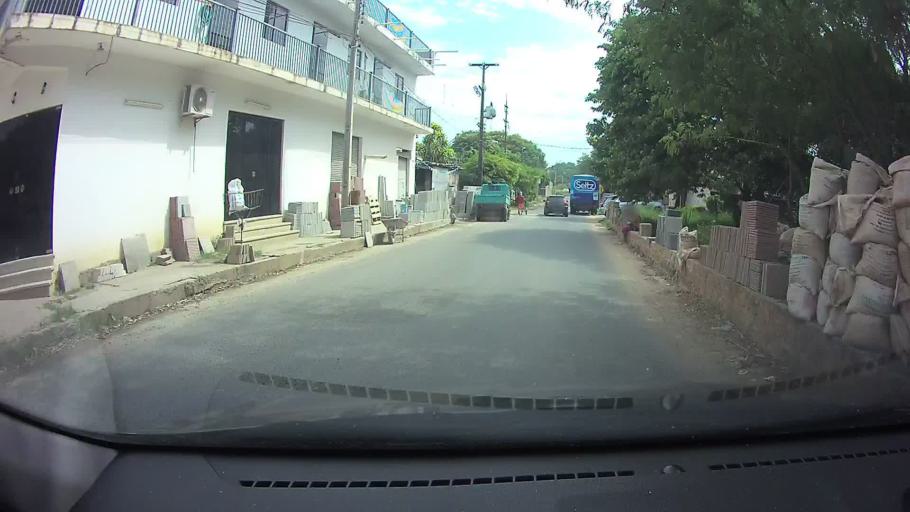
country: PY
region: Central
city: Fernando de la Mora
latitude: -25.2967
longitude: -57.5367
